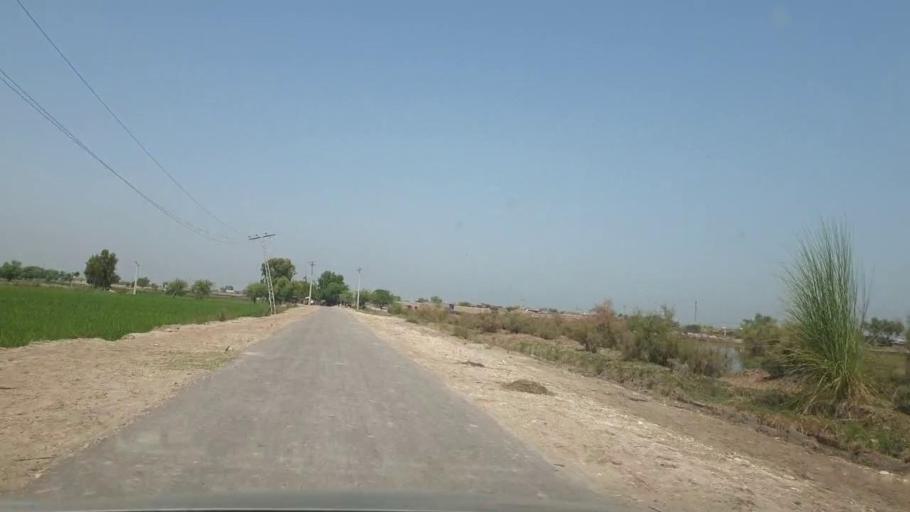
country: PK
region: Sindh
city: Warah
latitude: 27.4780
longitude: 67.7570
